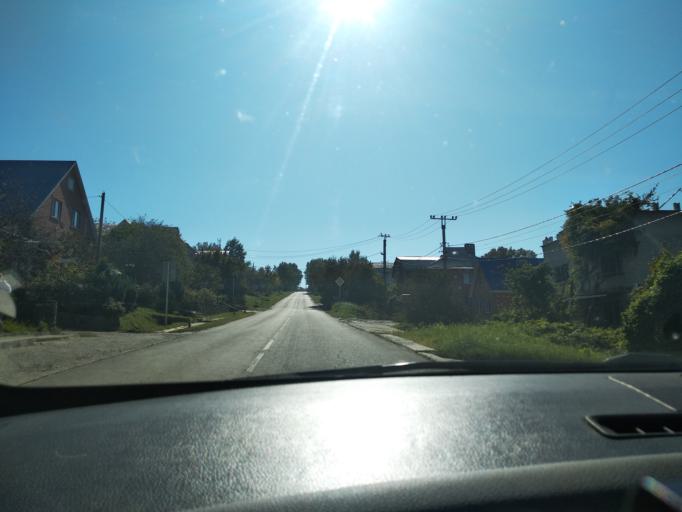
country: RU
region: Krasnodarskiy
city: Goryachiy Klyuch
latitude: 44.6266
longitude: 39.1570
